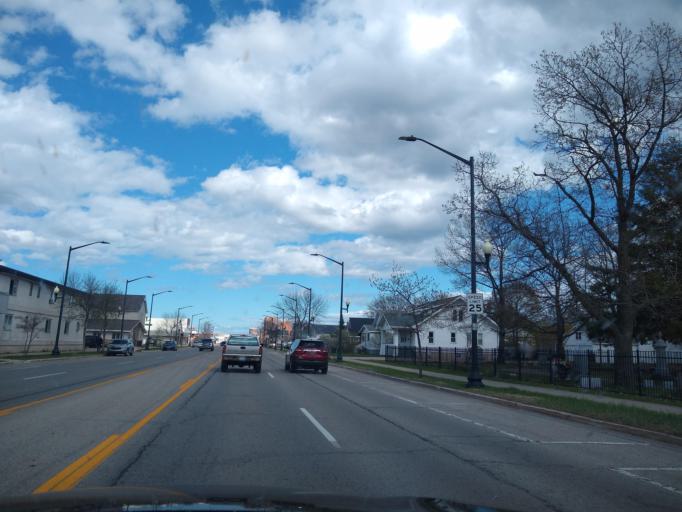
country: US
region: Michigan
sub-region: Delta County
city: Escanaba
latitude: 45.7457
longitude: -87.0756
